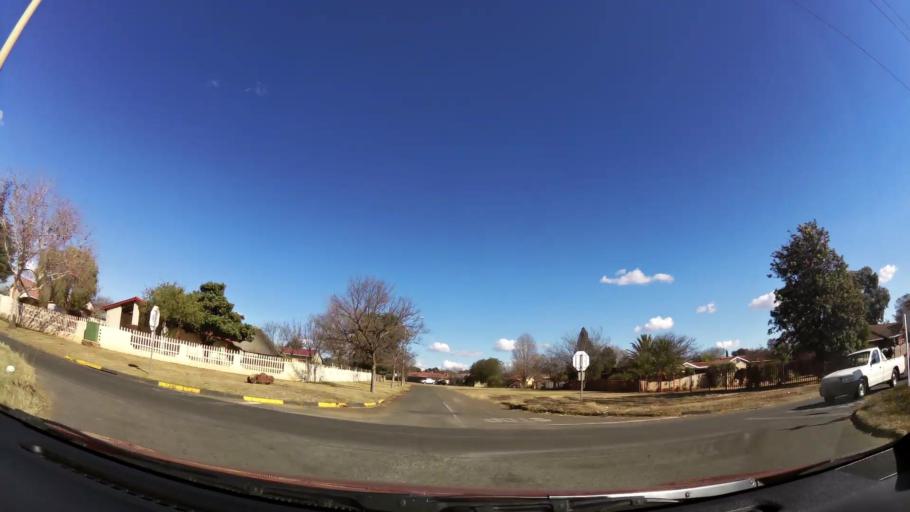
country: ZA
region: Gauteng
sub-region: West Rand District Municipality
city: Carletonville
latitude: -26.3696
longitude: 27.3855
